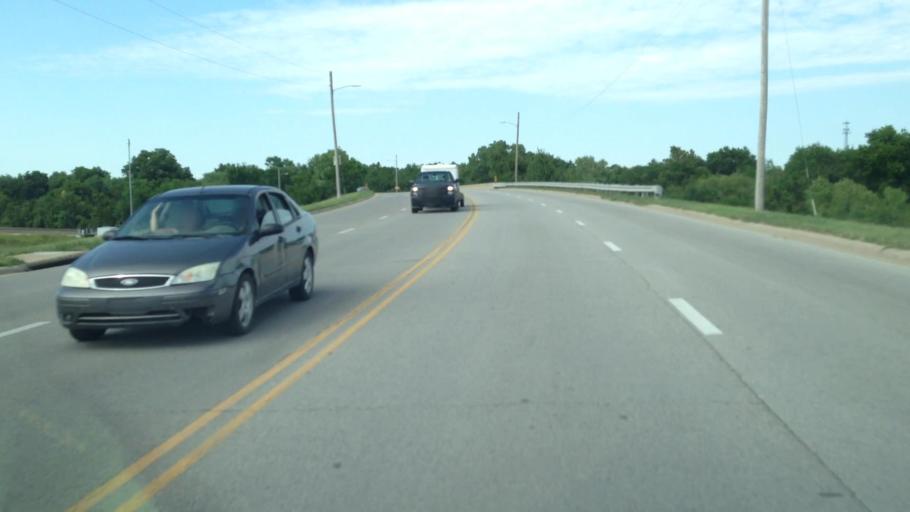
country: US
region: Kansas
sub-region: Labette County
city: Parsons
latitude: 37.3270
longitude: -95.2608
